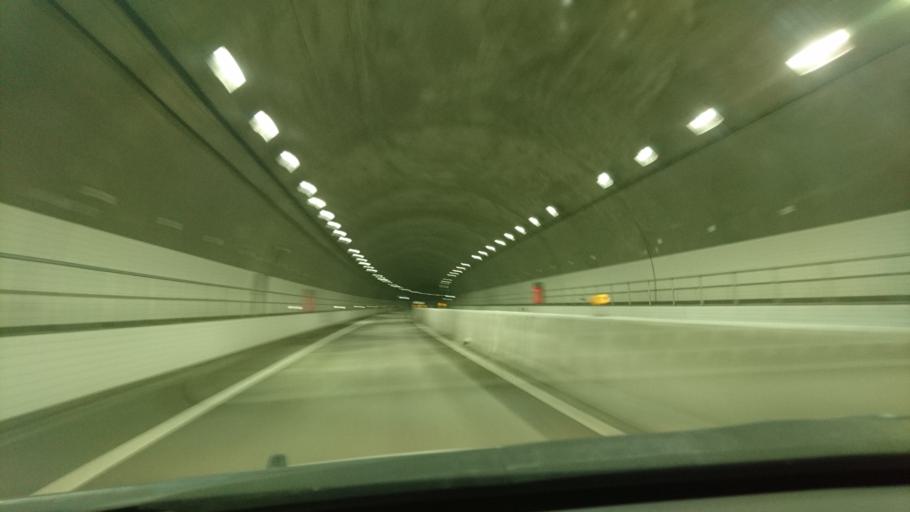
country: JP
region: Iwate
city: Miyako
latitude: 39.8062
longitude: 141.9554
